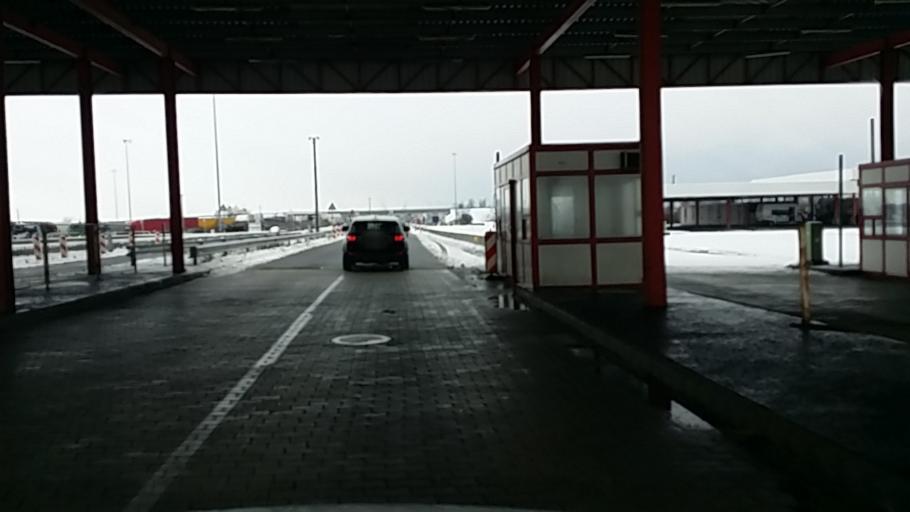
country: HU
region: Gyor-Moson-Sopron
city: Rajka
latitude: 48.0096
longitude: 17.1780
